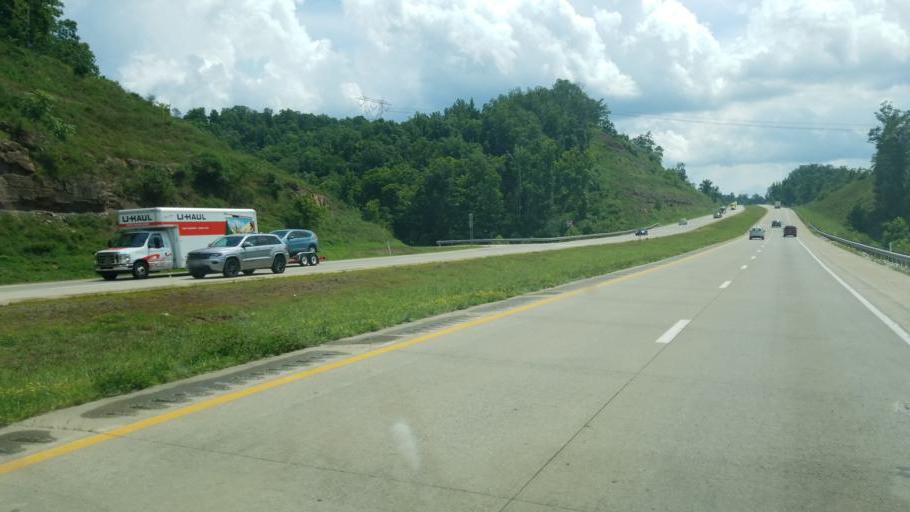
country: US
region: West Virginia
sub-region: Putnam County
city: Eleanor
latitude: 38.5130
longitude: -81.9324
